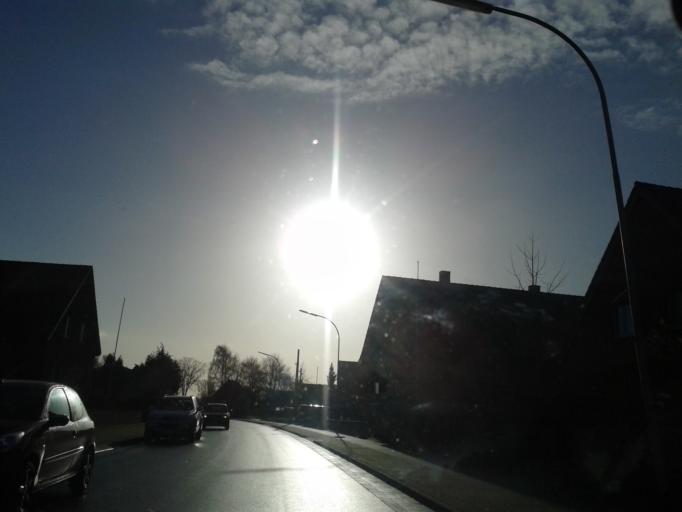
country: DE
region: North Rhine-Westphalia
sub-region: Regierungsbezirk Dusseldorf
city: Xanten
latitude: 51.7018
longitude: 6.4130
